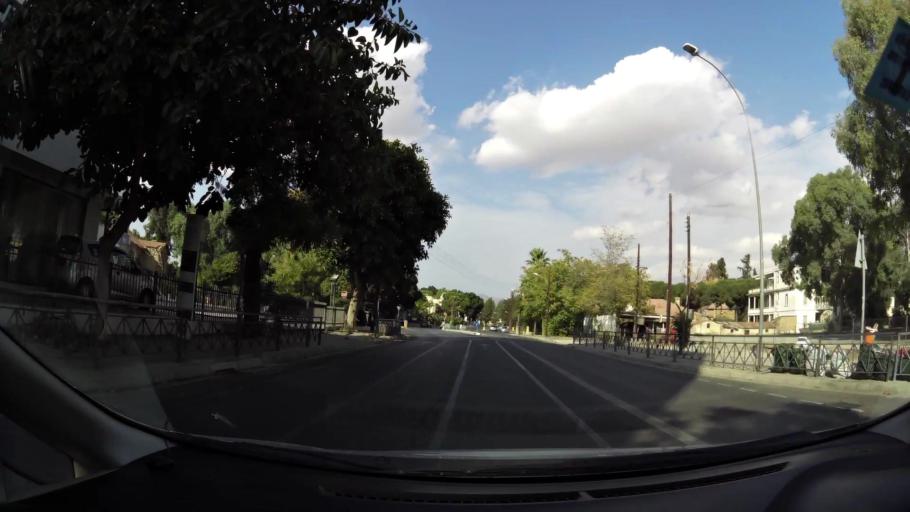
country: CY
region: Lefkosia
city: Nicosia
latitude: 35.1707
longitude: 33.3546
